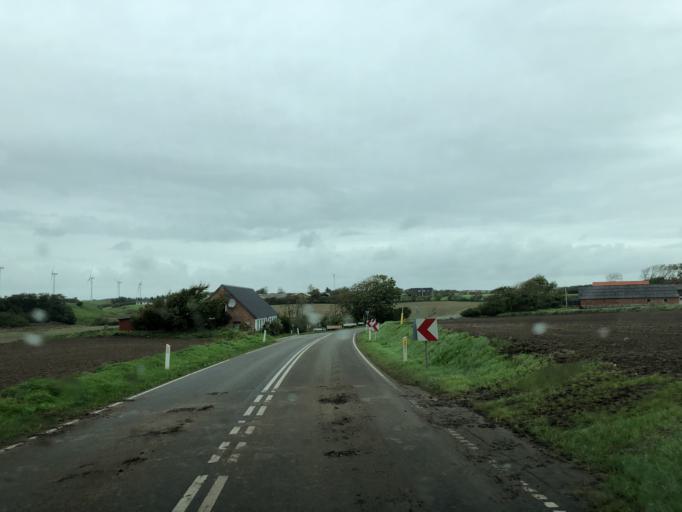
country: DK
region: North Denmark
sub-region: Thisted Kommune
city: Hurup
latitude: 56.7180
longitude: 8.3890
